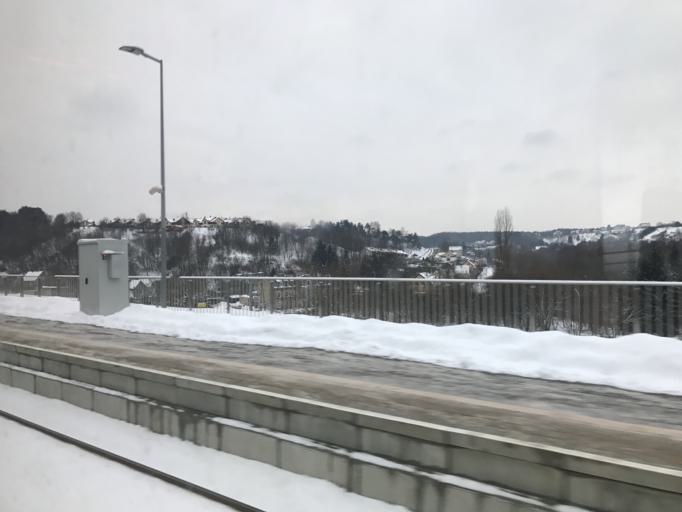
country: PL
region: Pomeranian Voivodeship
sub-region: Powiat gdanski
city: Kowale
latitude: 54.3656
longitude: 18.5737
